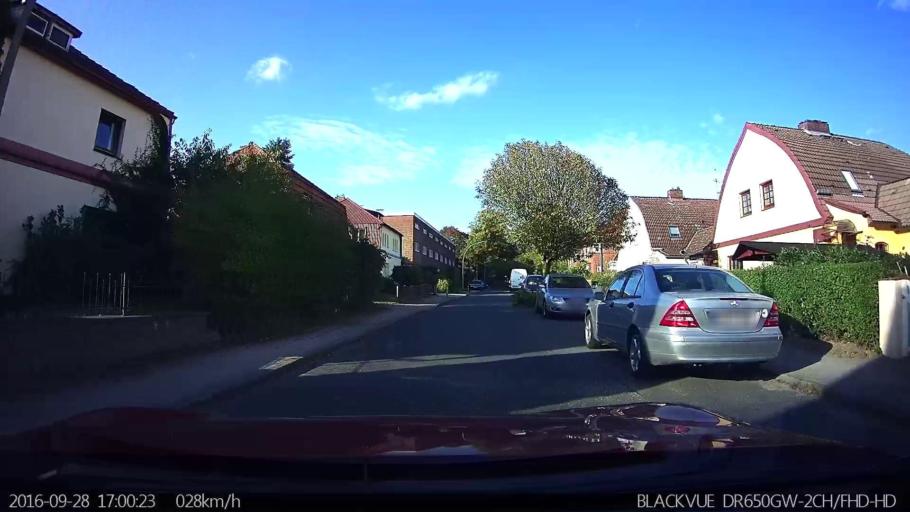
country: DE
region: Hamburg
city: Eidelstedt
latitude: 53.5708
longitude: 9.8803
